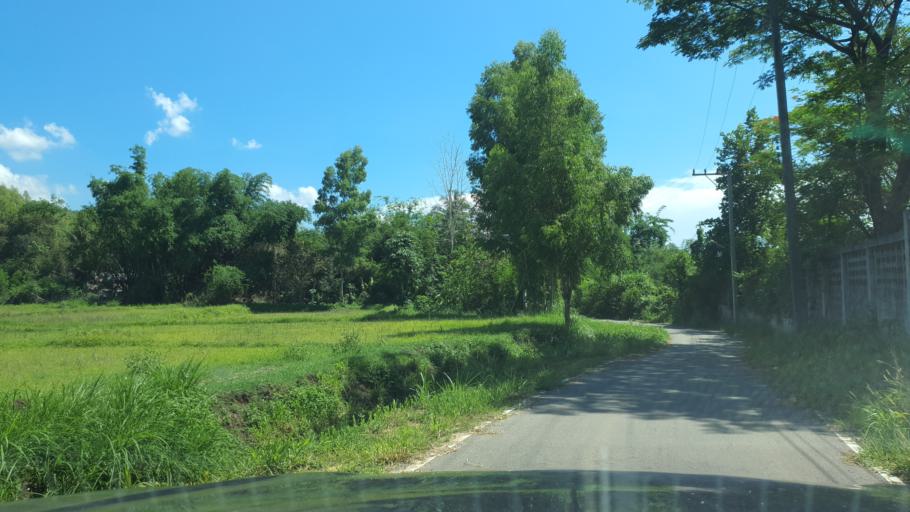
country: TH
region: Chiang Mai
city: Mae On
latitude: 18.7991
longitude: 99.2661
